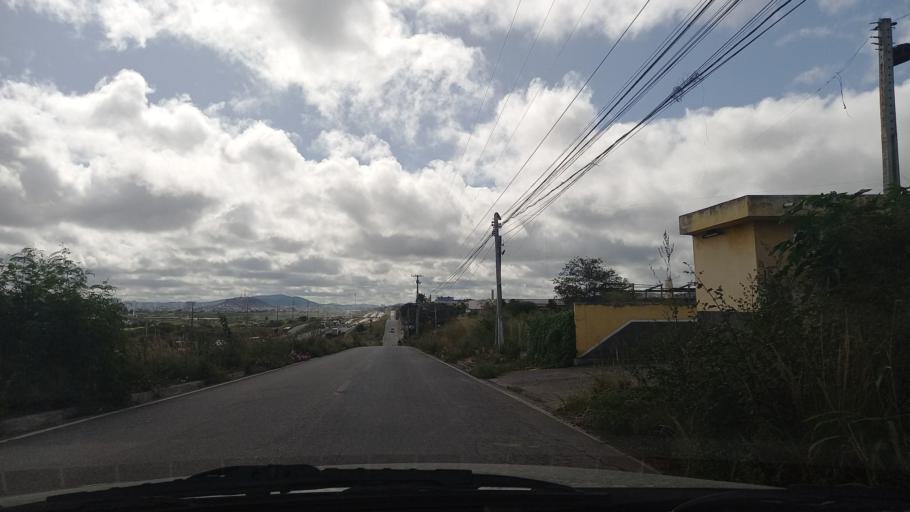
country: BR
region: Pernambuco
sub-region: Caruaru
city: Caruaru
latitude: -8.3076
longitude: -36.0196
